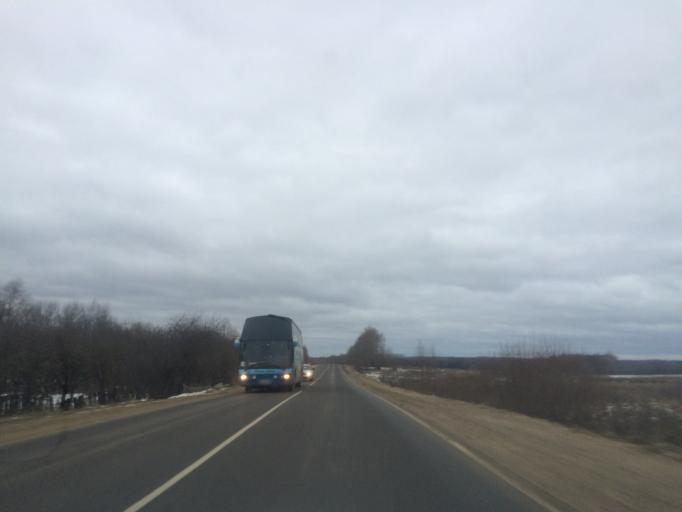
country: RU
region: Tula
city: Odoyev
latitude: 53.9948
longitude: 36.7362
